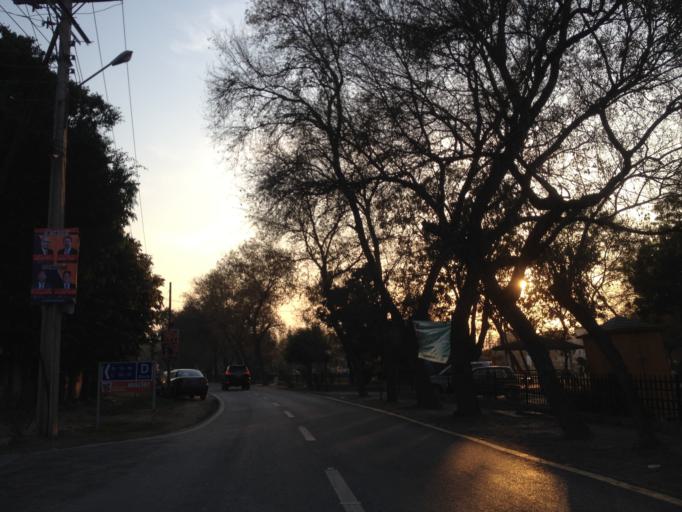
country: PK
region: Punjab
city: Lahore
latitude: 31.4909
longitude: 74.3142
